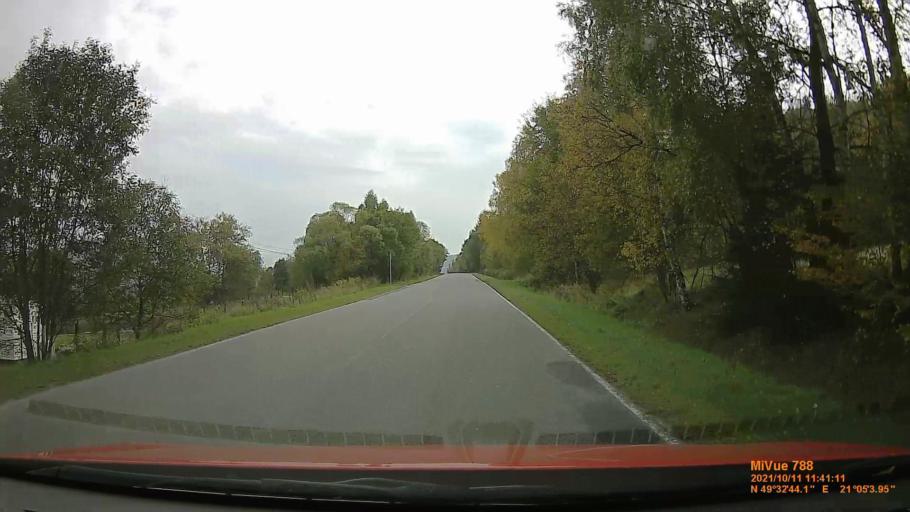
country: PL
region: Lesser Poland Voivodeship
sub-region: Powiat gorlicki
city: Uscie Gorlickie
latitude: 49.5455
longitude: 21.0846
